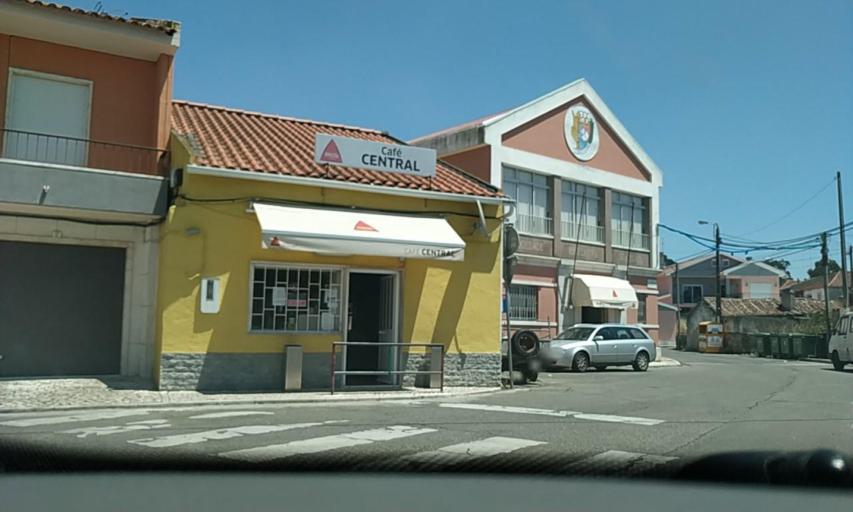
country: PT
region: Lisbon
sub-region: Sintra
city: Pero Pinheiro
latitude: 38.8660
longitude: -9.3143
